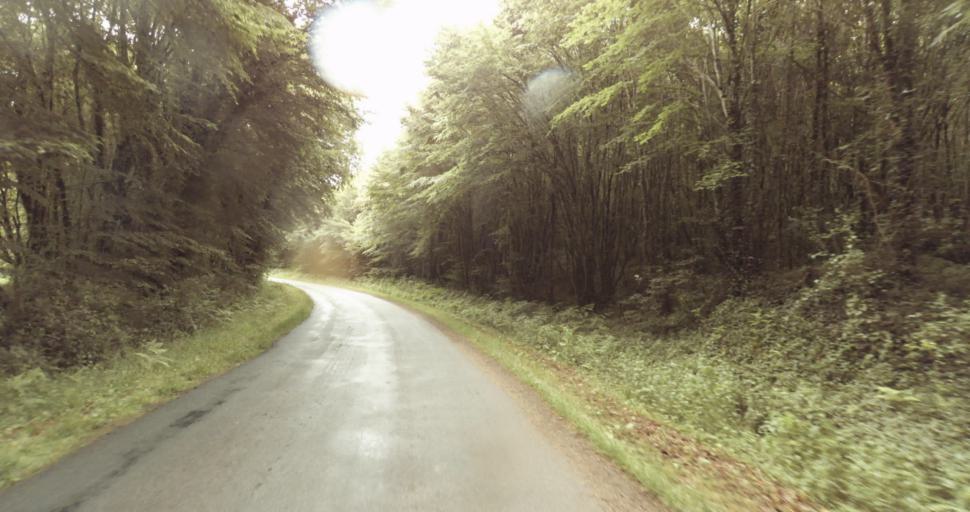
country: FR
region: Aquitaine
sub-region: Departement de la Dordogne
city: Belves
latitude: 44.7523
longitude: 0.9438
